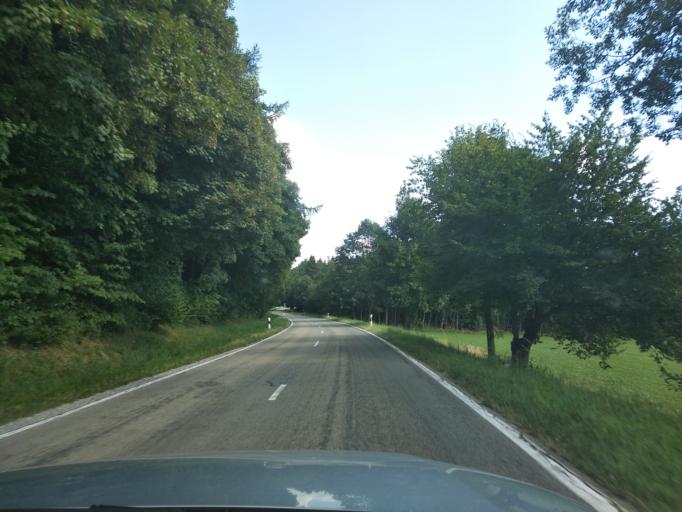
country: DE
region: Baden-Wuerttemberg
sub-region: Tuebingen Region
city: Leutkirch im Allgau
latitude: 47.8811
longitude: 9.9862
